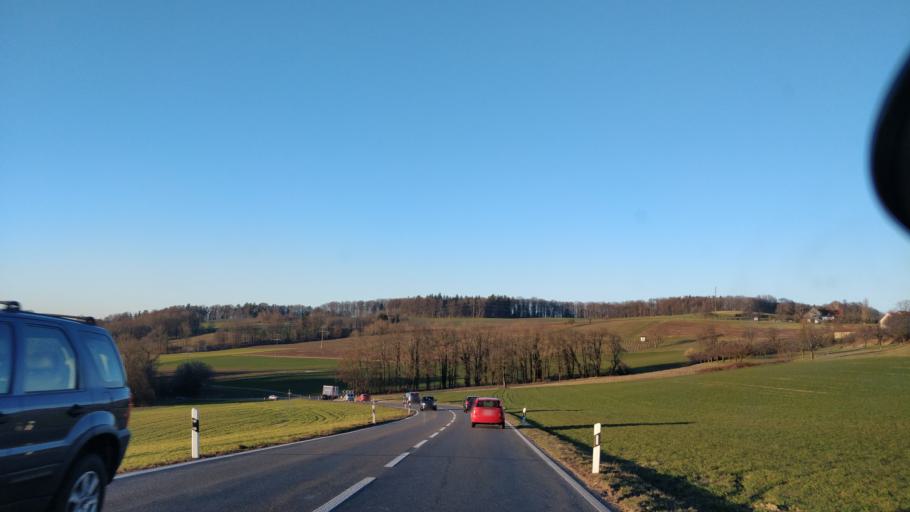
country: CH
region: Zurich
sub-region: Bezirk Buelach
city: Buelach / Seematt
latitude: 47.5145
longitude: 8.5615
